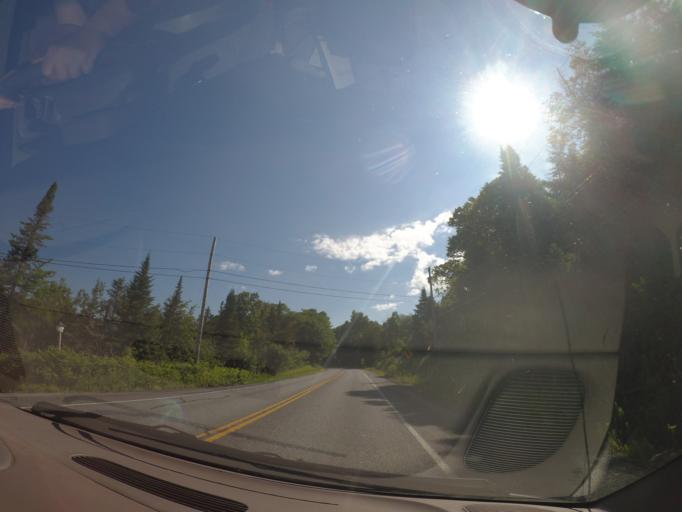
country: US
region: Vermont
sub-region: Bennington County
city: Bennington
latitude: 42.8903
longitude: -73.0648
